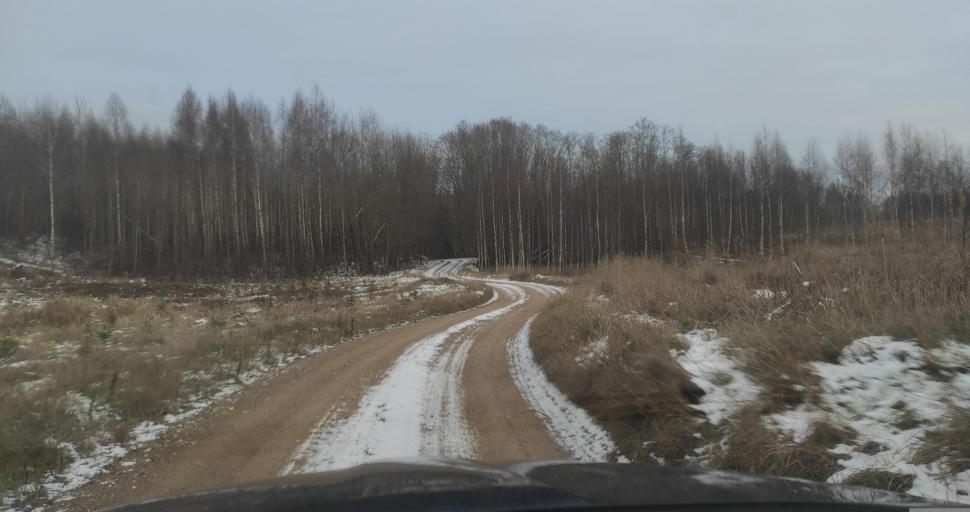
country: LV
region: Alsunga
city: Alsunga
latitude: 56.9575
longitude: 21.6440
